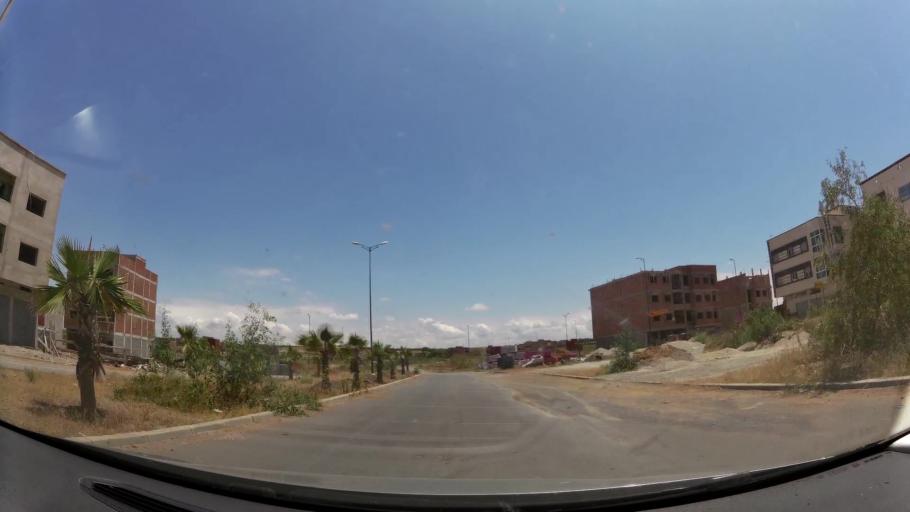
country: MA
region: Gharb-Chrarda-Beni Hssen
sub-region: Kenitra Province
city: Kenitra
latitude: 34.2449
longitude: -6.6528
